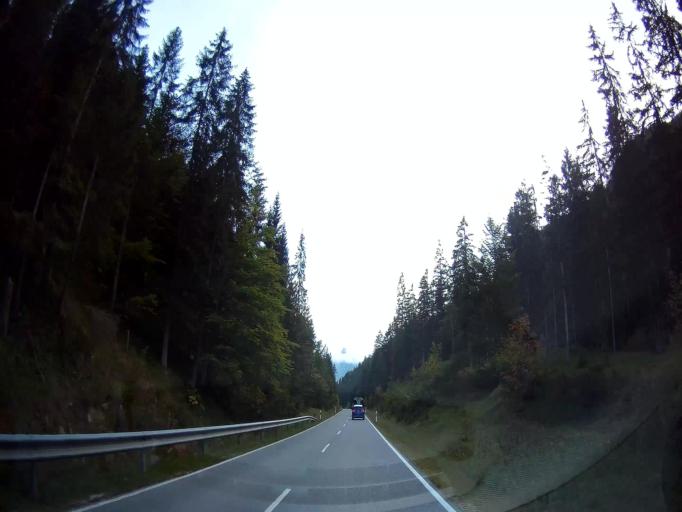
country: DE
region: Bavaria
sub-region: Upper Bavaria
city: Ramsau
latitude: 47.6380
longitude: 12.9124
